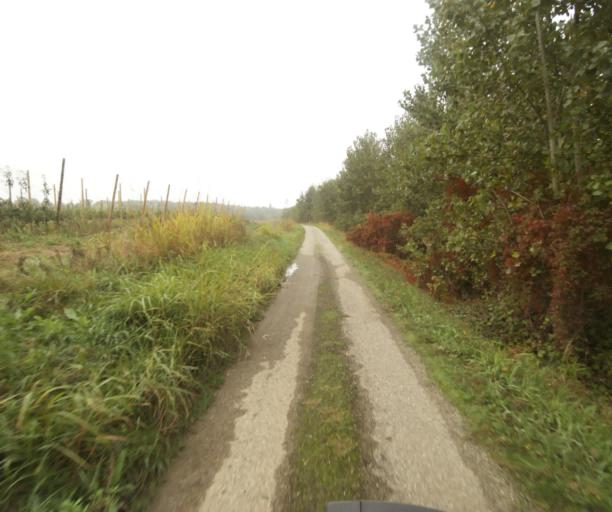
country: FR
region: Midi-Pyrenees
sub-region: Departement du Tarn-et-Garonne
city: Orgueil
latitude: 43.9109
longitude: 1.4204
